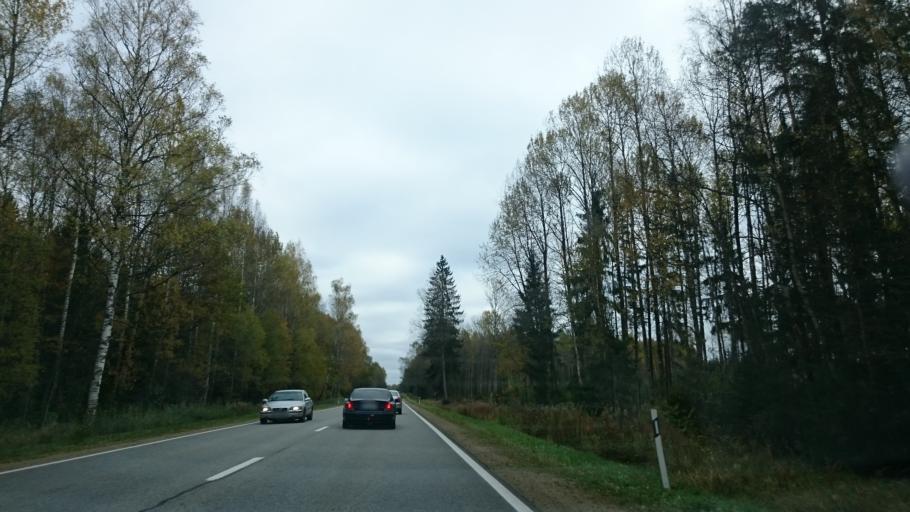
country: LV
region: Ligatne
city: Ligatne
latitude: 57.1823
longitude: 25.0046
